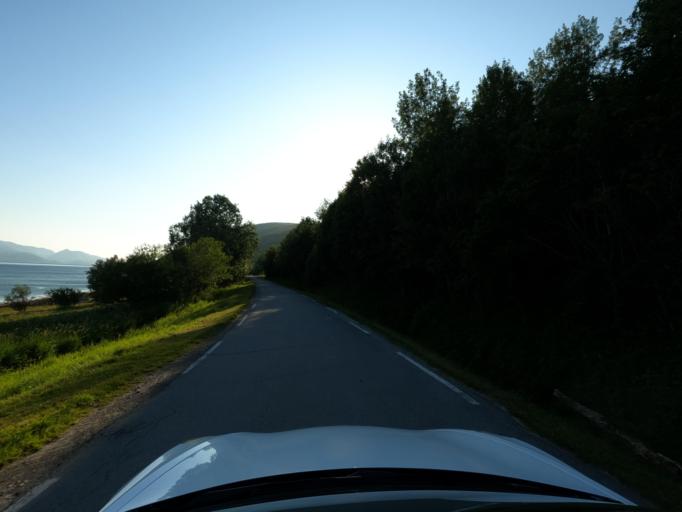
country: NO
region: Nordland
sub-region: Ballangen
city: Ballangen
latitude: 68.4683
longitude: 16.8009
